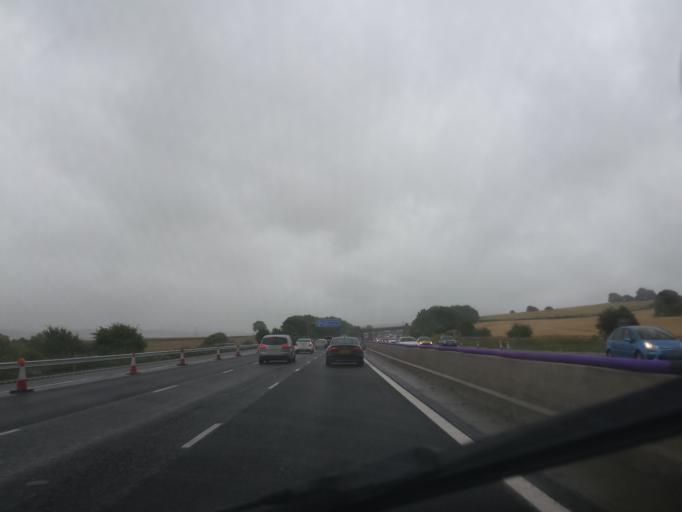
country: GB
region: England
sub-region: Derbyshire
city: Bolsover
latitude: 53.2201
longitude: -1.3278
